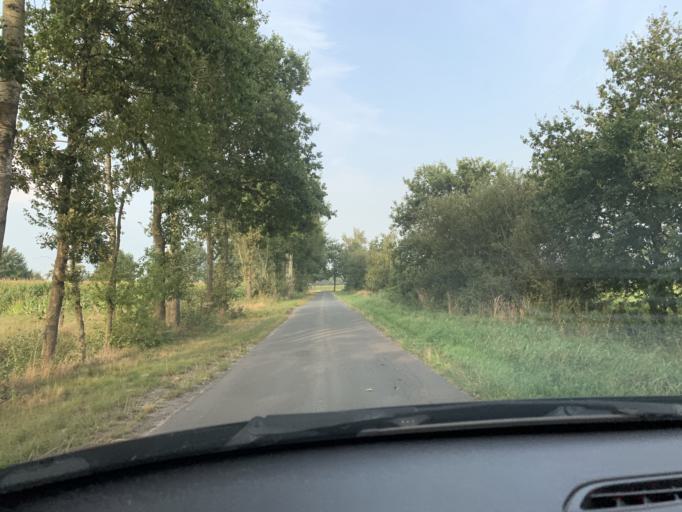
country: DE
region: Lower Saxony
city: Apen
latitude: 53.2424
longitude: 7.8272
